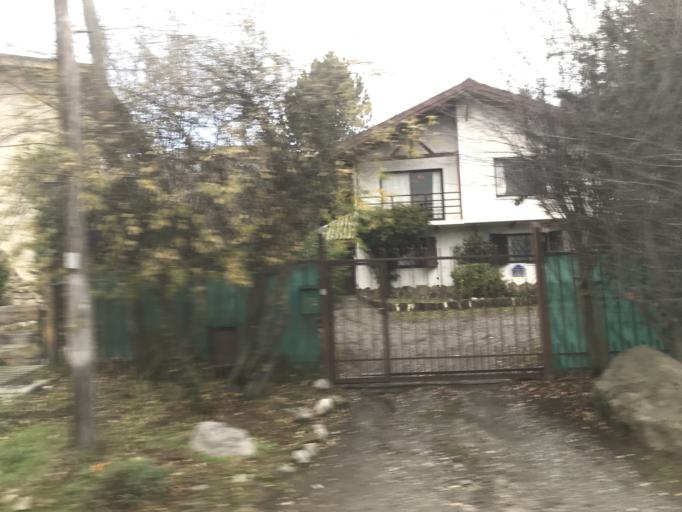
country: AR
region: Rio Negro
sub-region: Departamento de Bariloche
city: San Carlos de Bariloche
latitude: -41.1326
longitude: -71.3543
